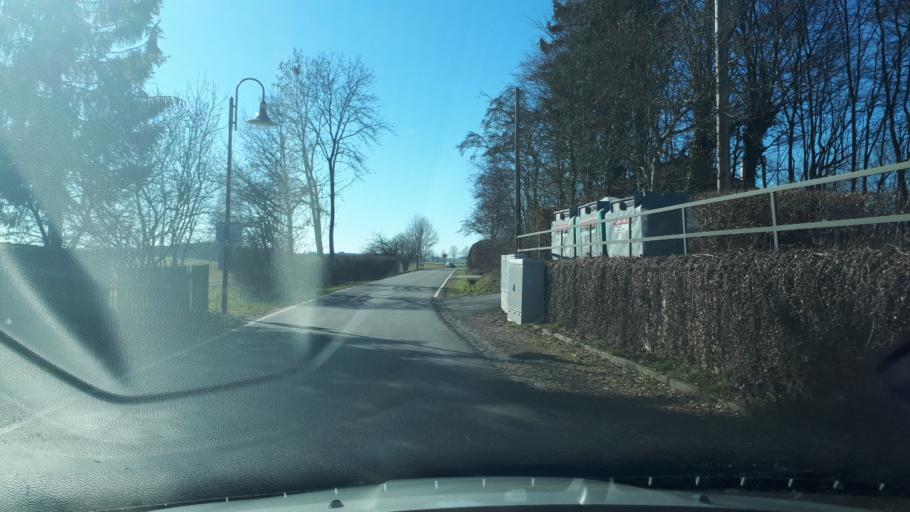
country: DE
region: Rheinland-Pfalz
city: Ellscheid
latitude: 50.1488
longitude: 6.9143
